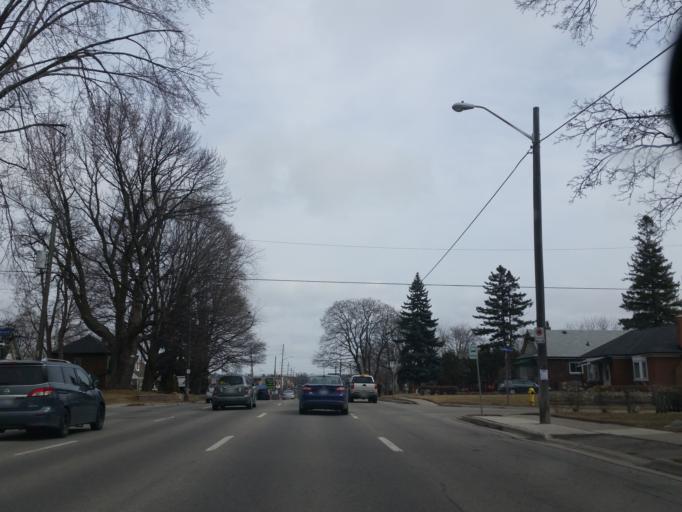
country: CA
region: Ontario
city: Oshawa
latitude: 43.9016
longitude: -78.8464
